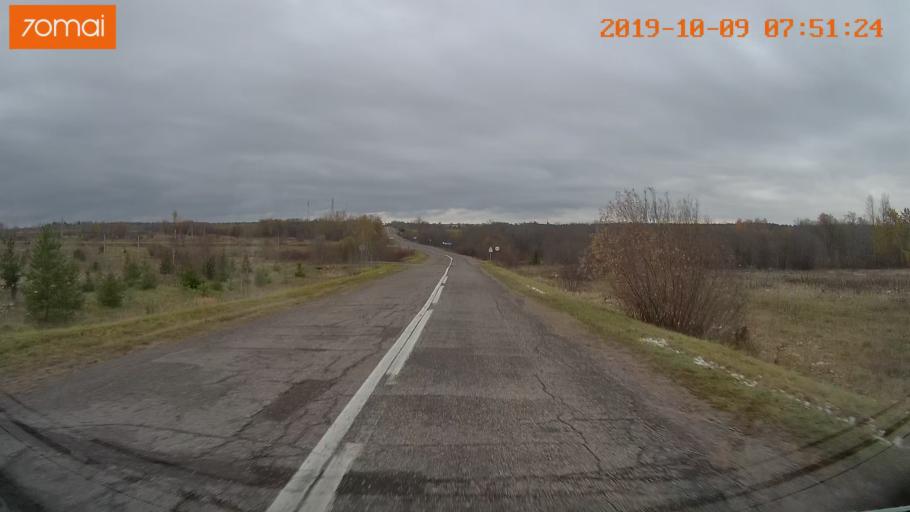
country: RU
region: Jaroslavl
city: Kukoboy
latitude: 58.6826
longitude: 39.8776
